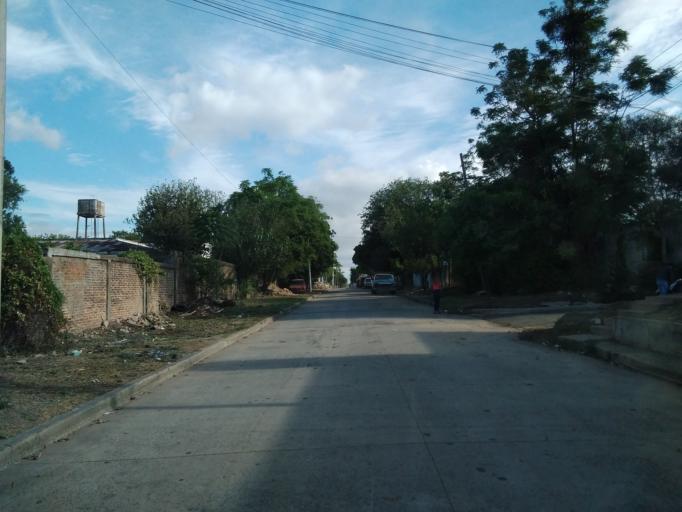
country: AR
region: Corrientes
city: Corrientes
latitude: -27.4628
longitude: -58.8122
